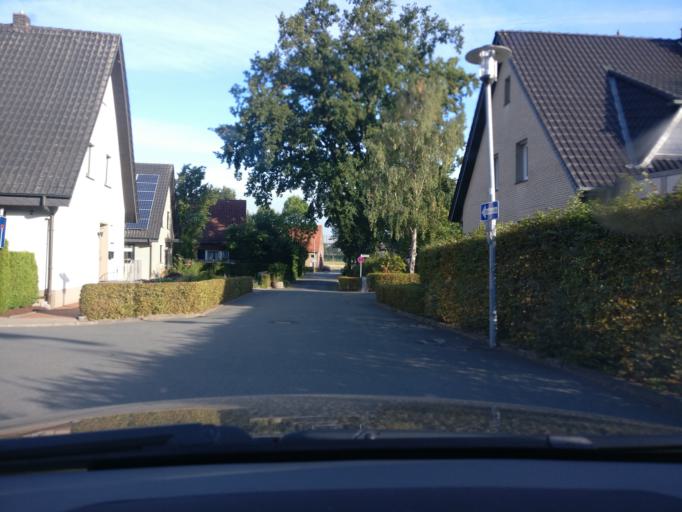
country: DE
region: Lower Saxony
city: Melle
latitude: 52.2115
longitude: 8.2693
